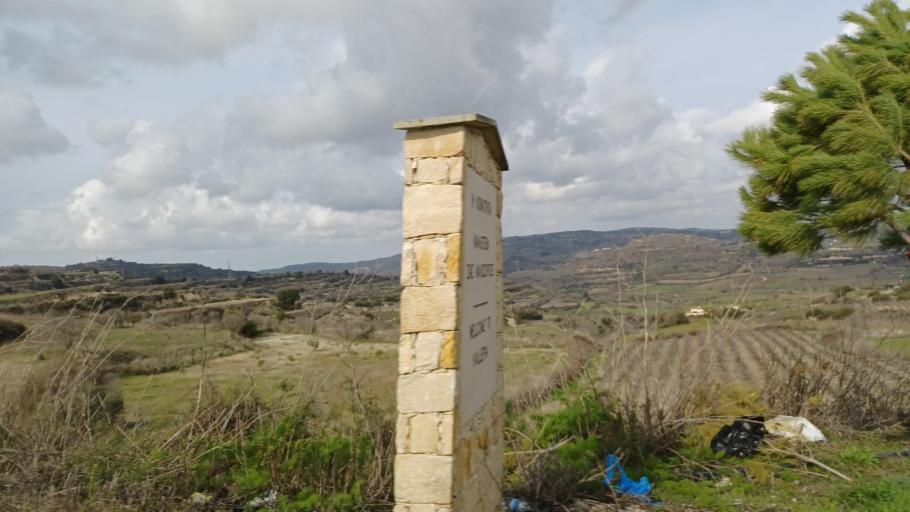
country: CY
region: Pafos
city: Mesogi
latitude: 34.8576
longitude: 32.4987
